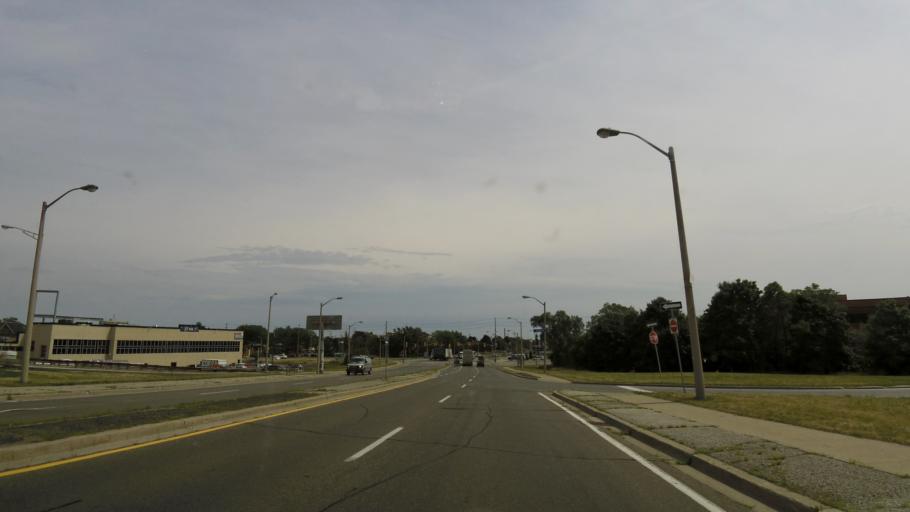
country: CA
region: Ontario
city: Etobicoke
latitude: 43.6196
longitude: -79.5126
